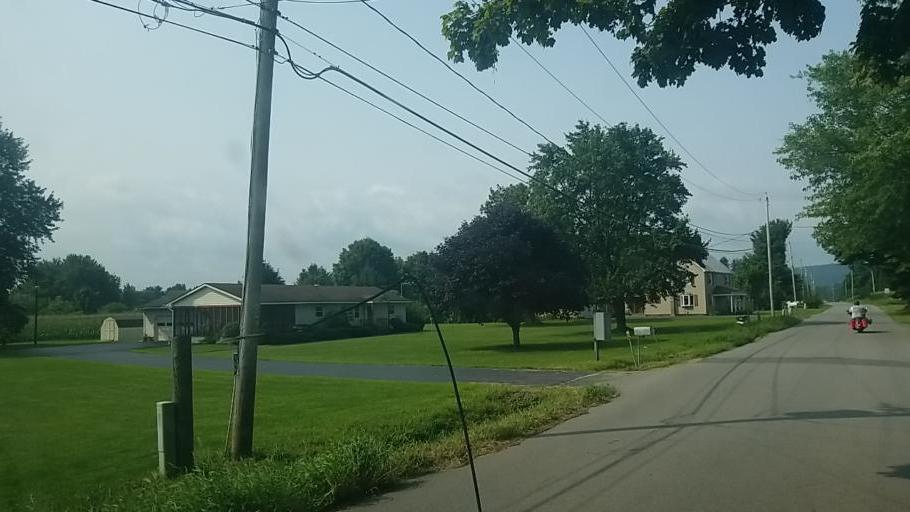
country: US
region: New York
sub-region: Montgomery County
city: Fonda
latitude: 42.9504
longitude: -74.4160
